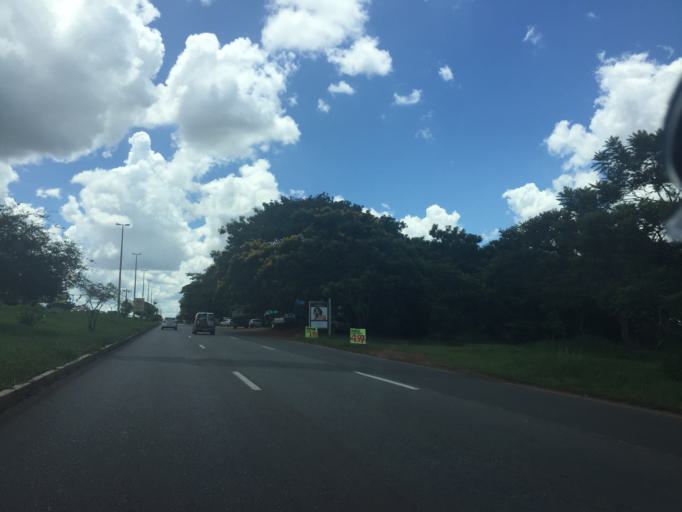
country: BR
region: Federal District
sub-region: Brasilia
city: Brasilia
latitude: -15.8679
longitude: -47.9458
